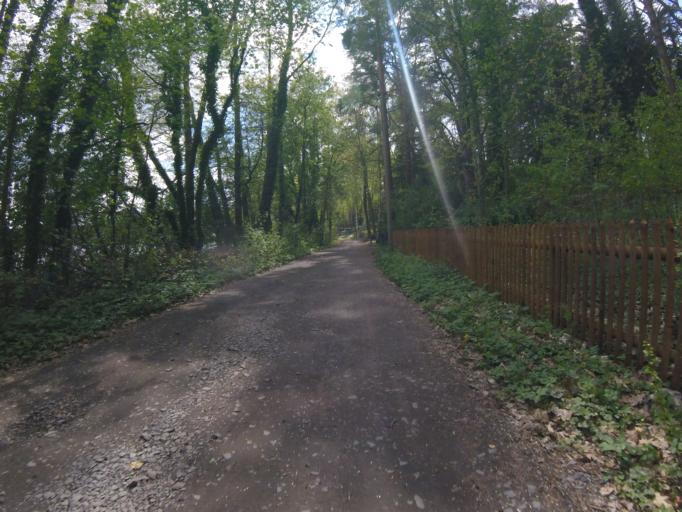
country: DE
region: Brandenburg
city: Teupitz
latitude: 52.1176
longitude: 13.6102
